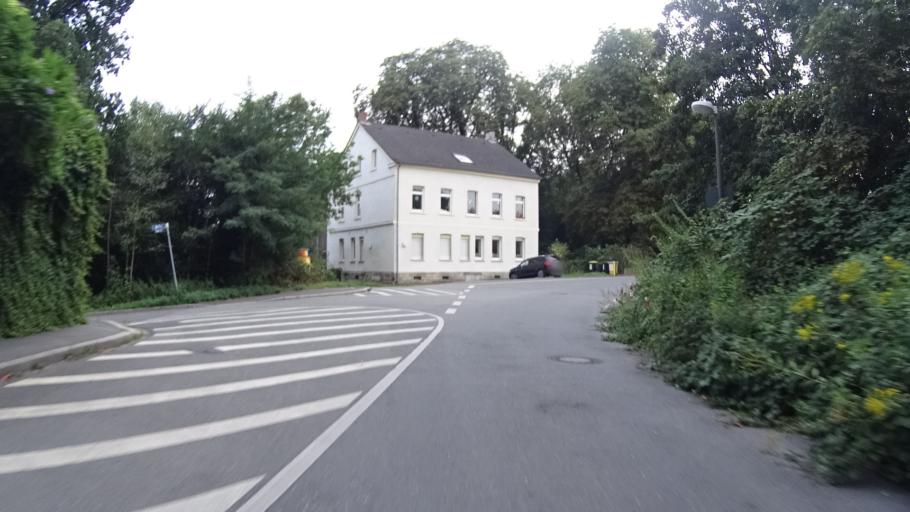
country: DE
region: North Rhine-Westphalia
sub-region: Regierungsbezirk Arnsberg
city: Dortmund
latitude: 51.4870
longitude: 7.4197
